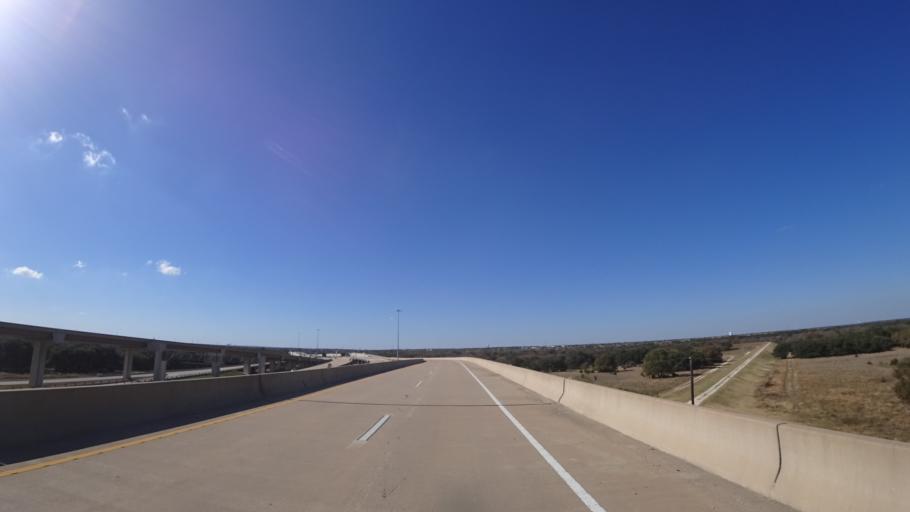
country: US
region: Texas
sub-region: Williamson County
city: Round Rock
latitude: 30.4794
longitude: -97.7110
